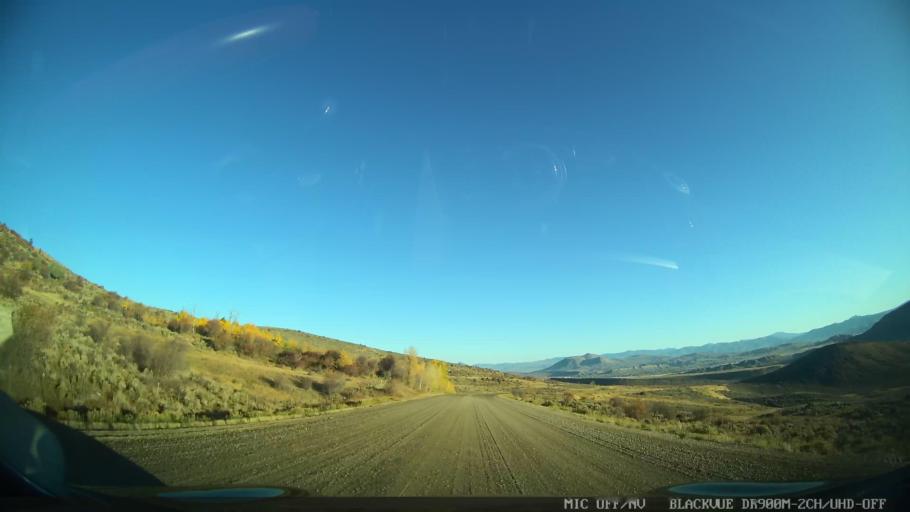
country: US
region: Colorado
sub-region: Grand County
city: Kremmling
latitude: 40.0016
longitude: -106.4056
